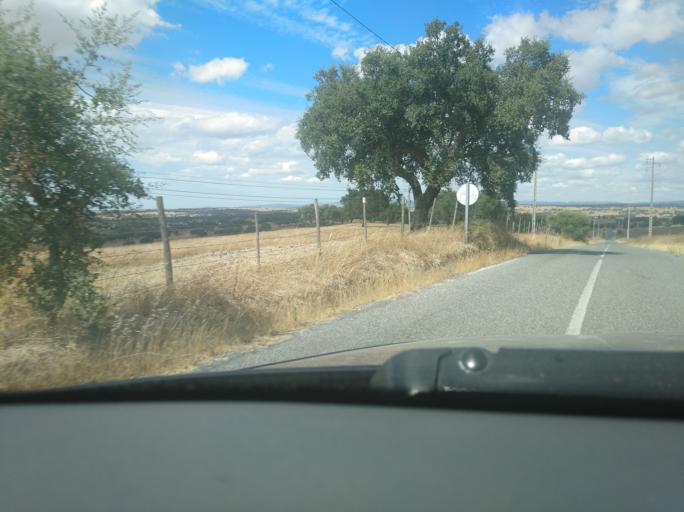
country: PT
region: Portalegre
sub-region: Arronches
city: Arronches
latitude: 39.0646
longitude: -7.4042
